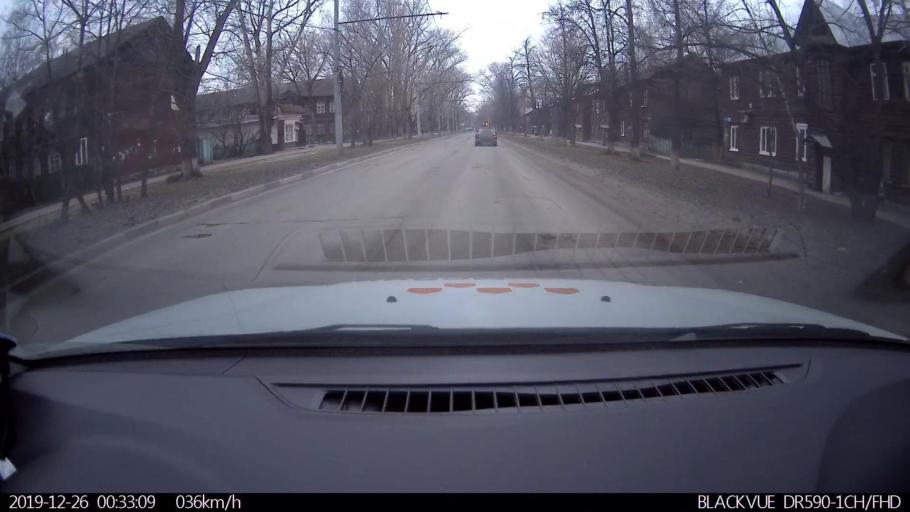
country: RU
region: Nizjnij Novgorod
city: Nizhniy Novgorod
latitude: 56.2879
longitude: 43.9232
